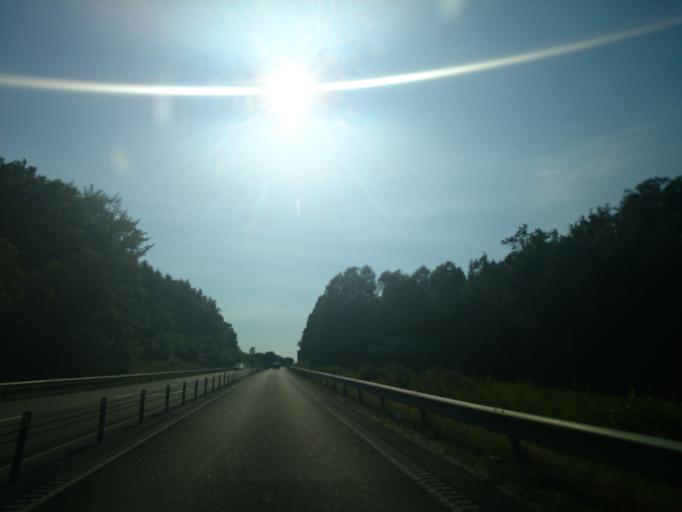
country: SE
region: Blekinge
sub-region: Karlshamns Kommun
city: Karlshamn
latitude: 56.1895
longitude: 14.9447
